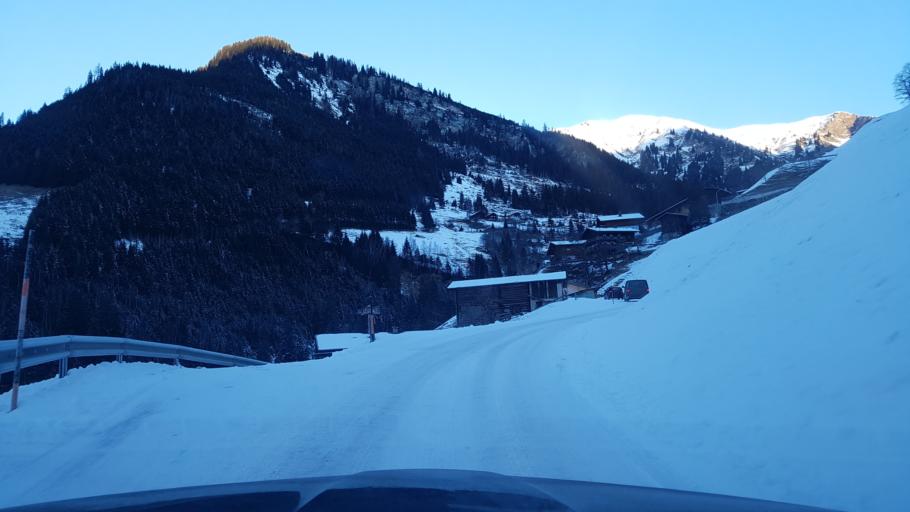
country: AT
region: Salzburg
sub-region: Politischer Bezirk Sankt Johann im Pongau
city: Huttschlag
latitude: 47.1702
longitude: 13.2660
